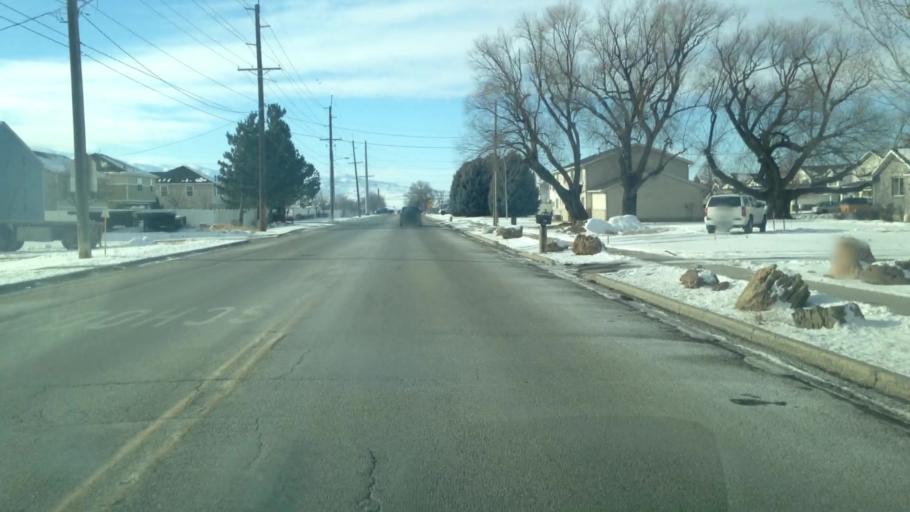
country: US
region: Utah
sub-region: Cache County
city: Logan
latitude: 41.7504
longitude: -111.8458
